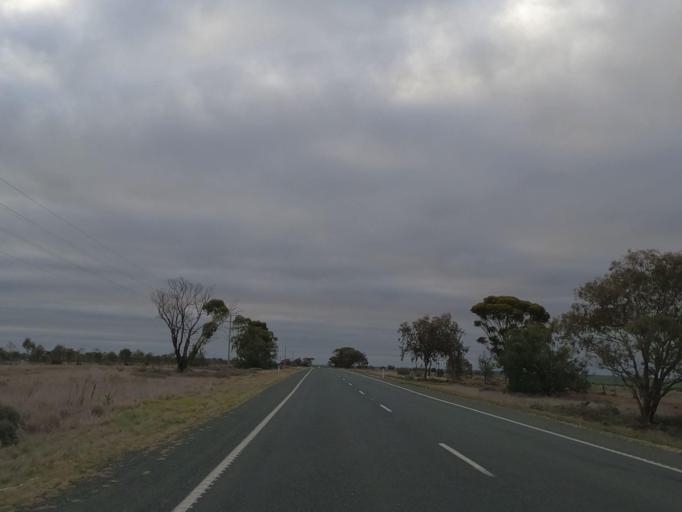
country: AU
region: Victoria
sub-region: Swan Hill
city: Swan Hill
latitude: -35.5713
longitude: 143.7862
